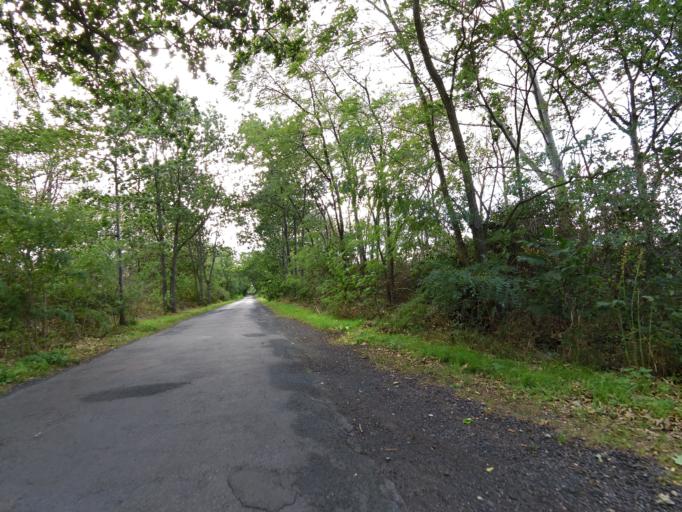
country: DE
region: Brandenburg
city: Grossbeeren
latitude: 52.3639
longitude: 13.3344
